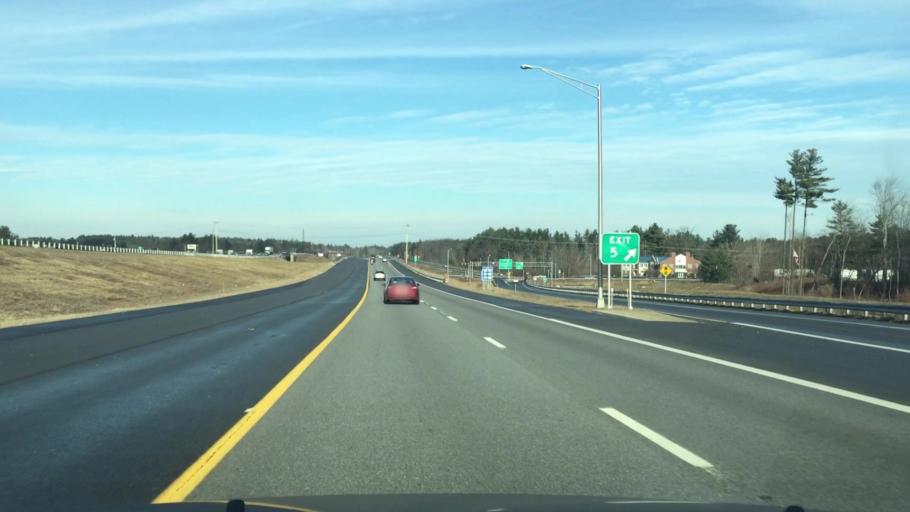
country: US
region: New Hampshire
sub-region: Rockingham County
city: Londonderry
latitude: 42.9130
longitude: -71.3688
